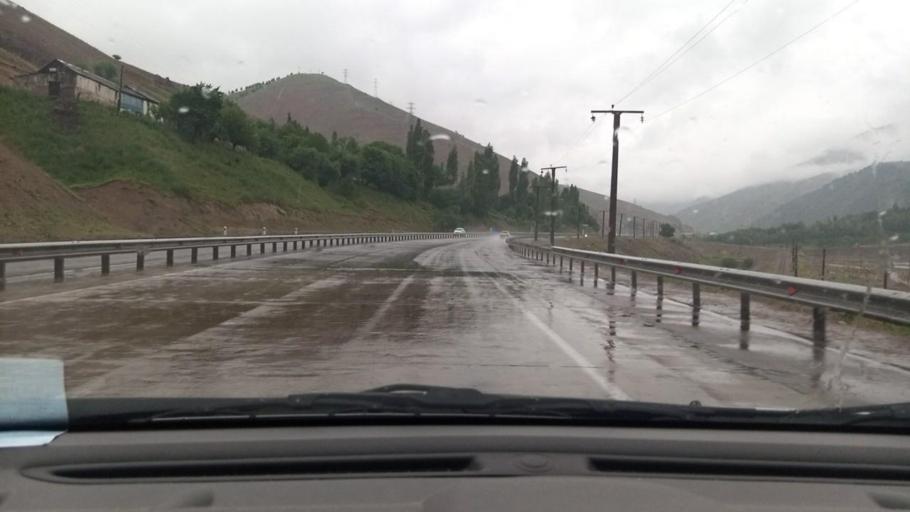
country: UZ
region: Toshkent
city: Angren
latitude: 41.1450
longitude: 70.4069
